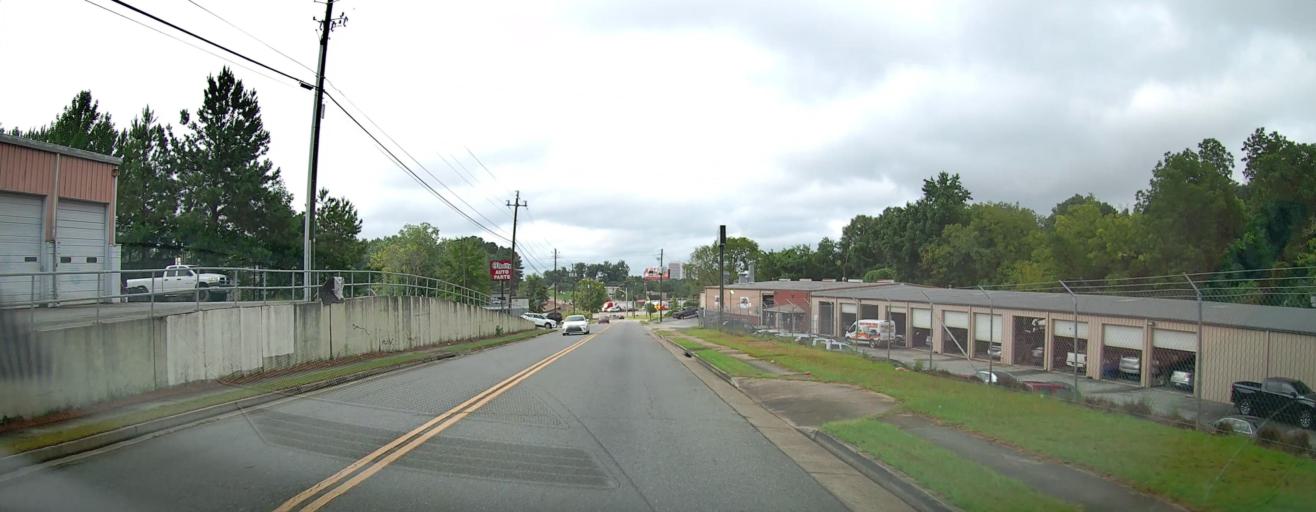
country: US
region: Georgia
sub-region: Bibb County
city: Macon
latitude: 32.8535
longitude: -83.6201
